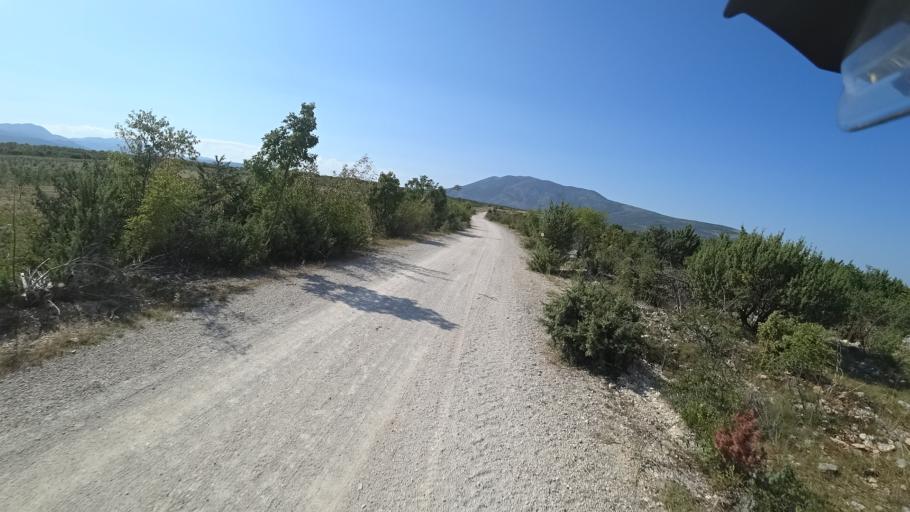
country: HR
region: Sibensko-Kniniska
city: Knin
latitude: 43.9941
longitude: 16.1932
